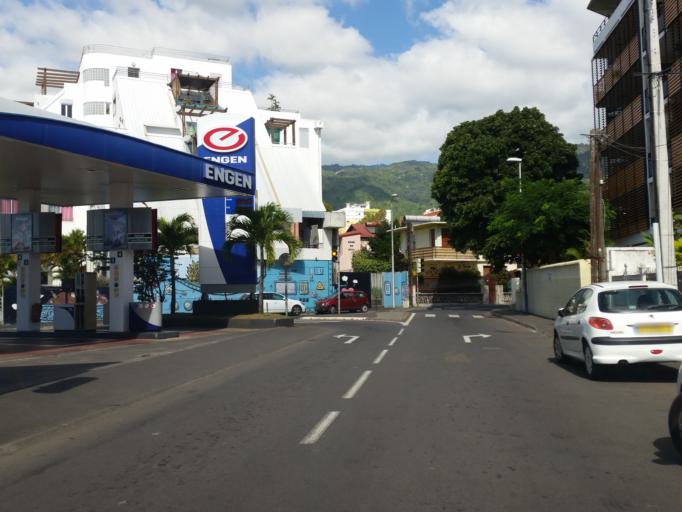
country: RE
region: Reunion
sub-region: Reunion
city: Saint-Denis
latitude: -20.8881
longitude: 55.4582
